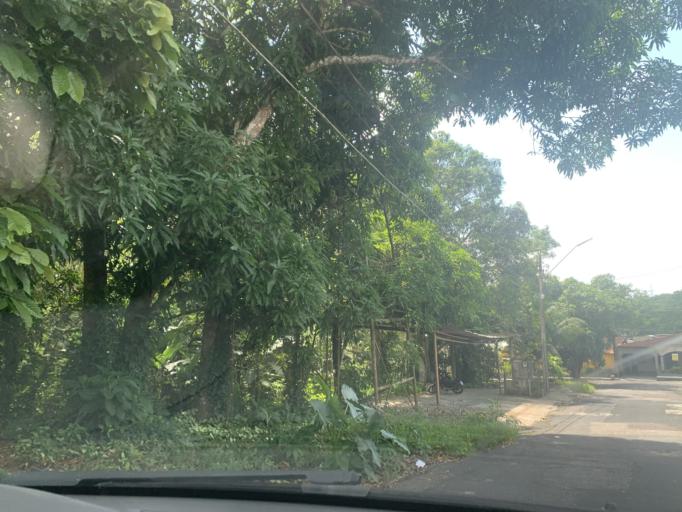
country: BR
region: Amazonas
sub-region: Manaus
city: Manaus
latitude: -3.1013
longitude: -59.9609
